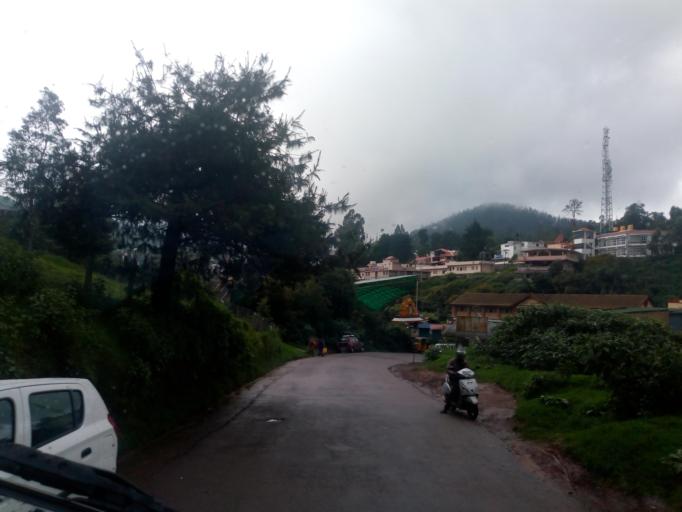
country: IN
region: Tamil Nadu
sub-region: Nilgiri
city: Ooty
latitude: 11.4122
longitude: 76.7102
